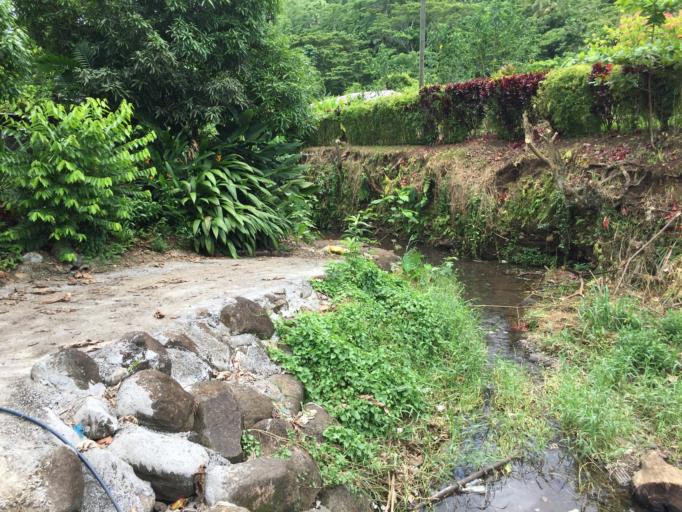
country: WS
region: Tuamasaga
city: Apia
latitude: -13.8564
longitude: -171.7828
